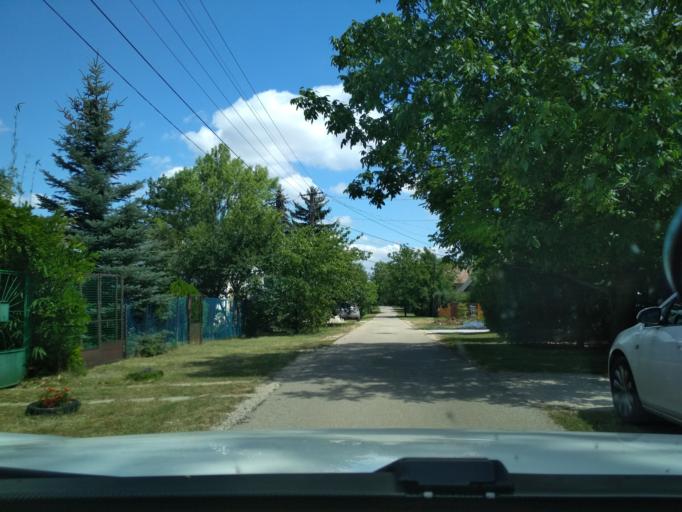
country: HU
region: Fejer
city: Gardony
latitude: 47.2112
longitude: 18.6585
